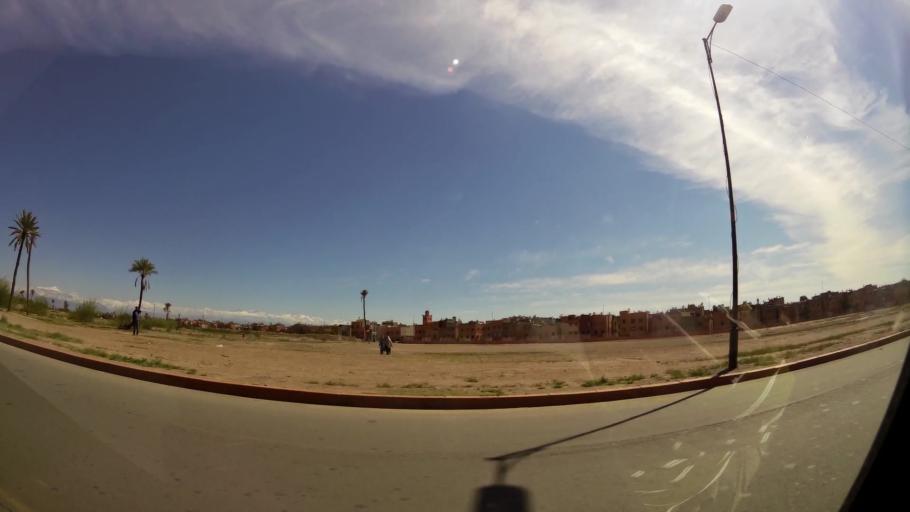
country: MA
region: Marrakech-Tensift-Al Haouz
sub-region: Marrakech
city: Marrakesh
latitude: 31.6209
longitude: -7.9655
